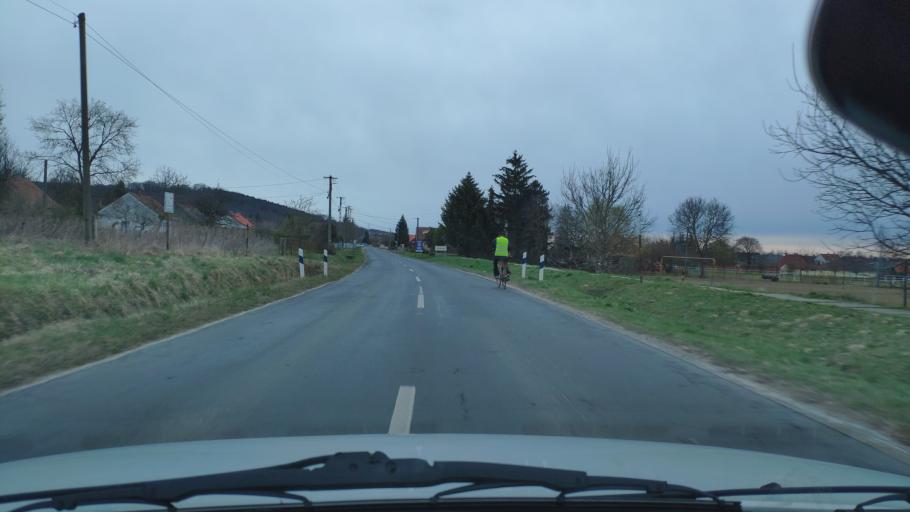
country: HU
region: Zala
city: Nagykanizsa
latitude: 46.5448
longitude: 16.9852
